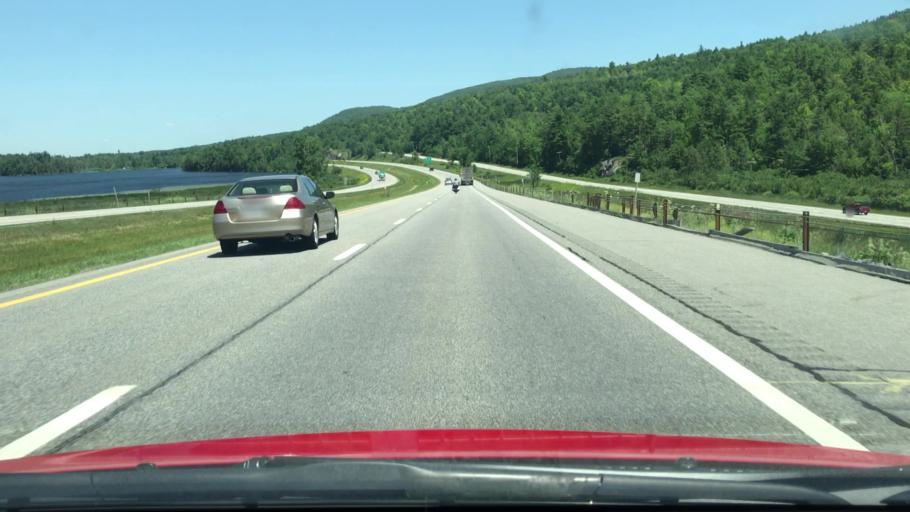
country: US
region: New York
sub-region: Essex County
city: Keeseville
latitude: 44.4204
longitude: -73.4953
